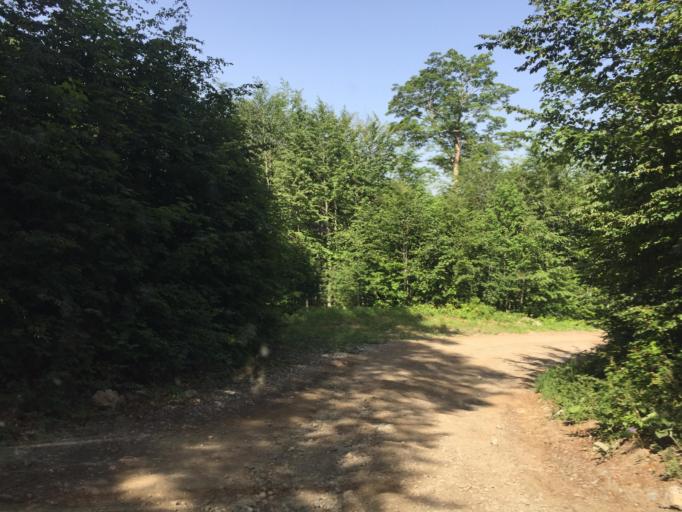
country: HR
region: Primorsko-Goranska
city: Podhum
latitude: 45.4308
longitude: 14.5806
